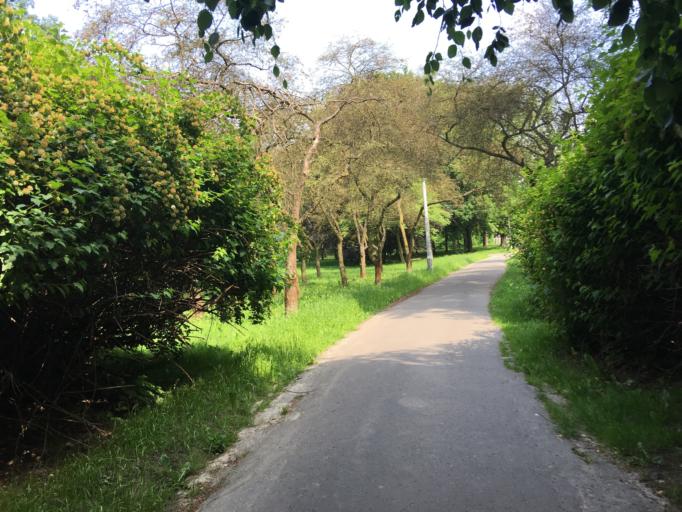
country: PL
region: Lesser Poland Voivodeship
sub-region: Krakow
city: Krakow
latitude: 50.0723
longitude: 19.9952
